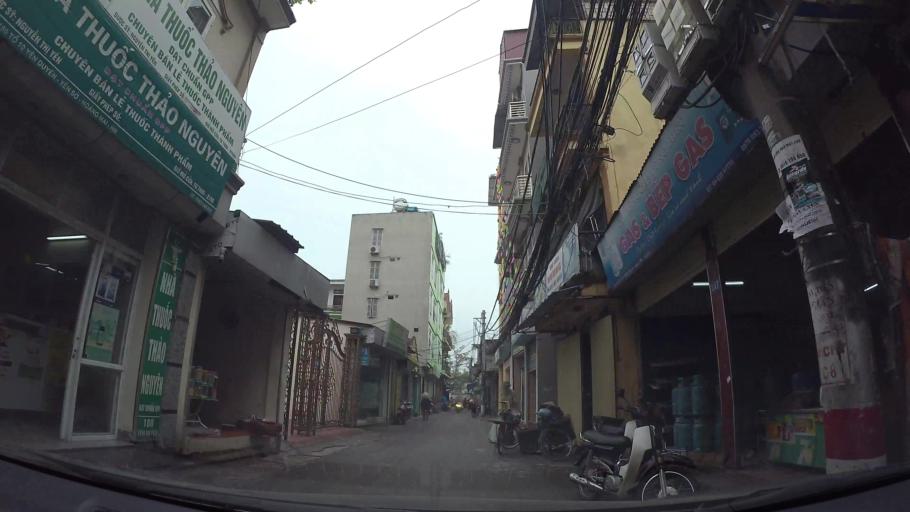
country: VN
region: Ha Noi
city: Van Dien
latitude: 20.9672
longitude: 105.8724
